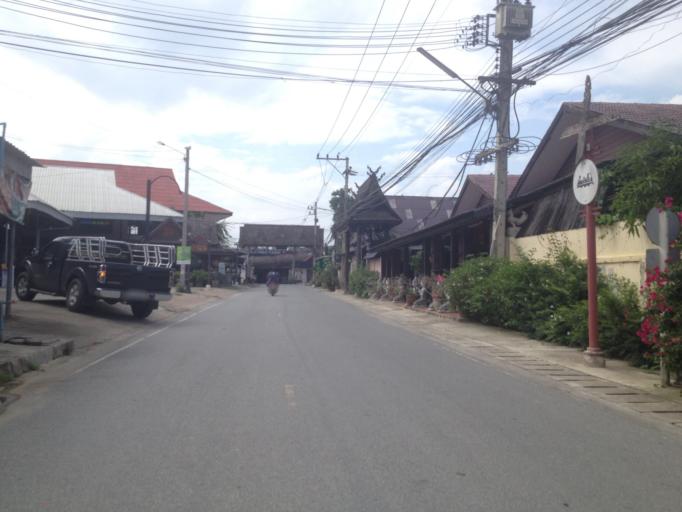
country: TH
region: Chiang Mai
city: Hang Dong
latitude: 18.6861
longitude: 98.9479
